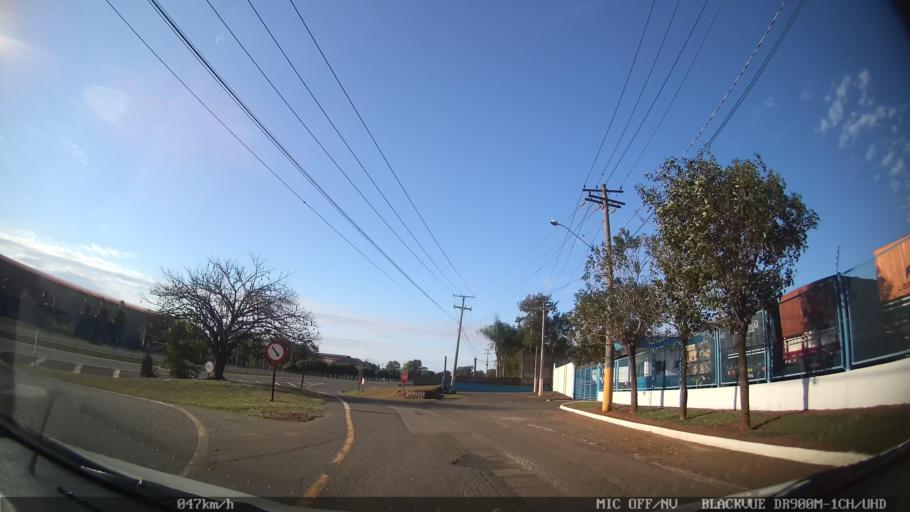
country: BR
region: Sao Paulo
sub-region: Piracicaba
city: Piracicaba
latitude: -22.6719
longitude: -47.6275
